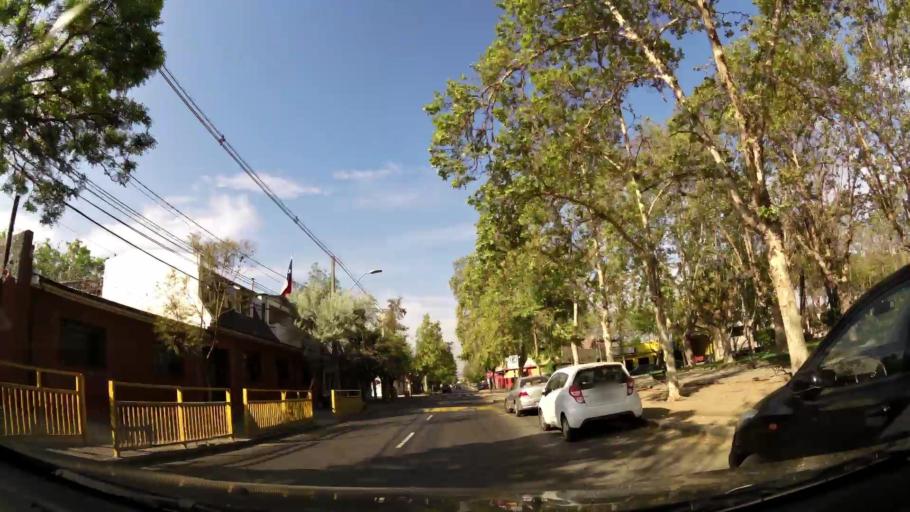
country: CL
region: Santiago Metropolitan
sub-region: Provincia de Maipo
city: San Bernardo
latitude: -33.6035
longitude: -70.7034
